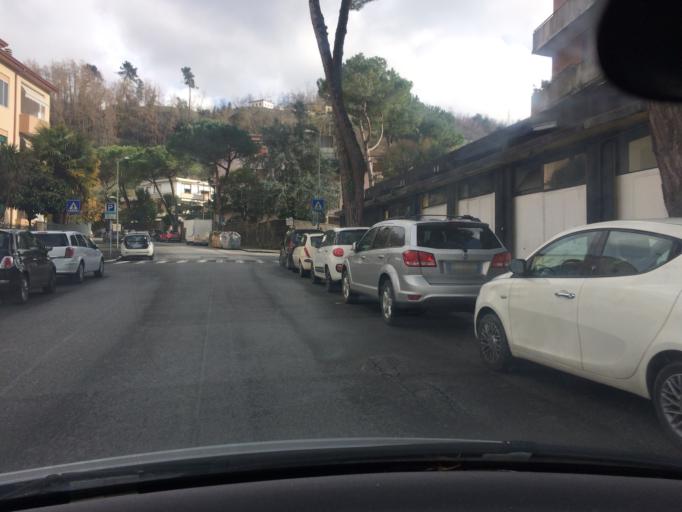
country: IT
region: Tuscany
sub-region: Provincia di Massa-Carrara
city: Carrara
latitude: 44.0747
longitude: 10.1008
